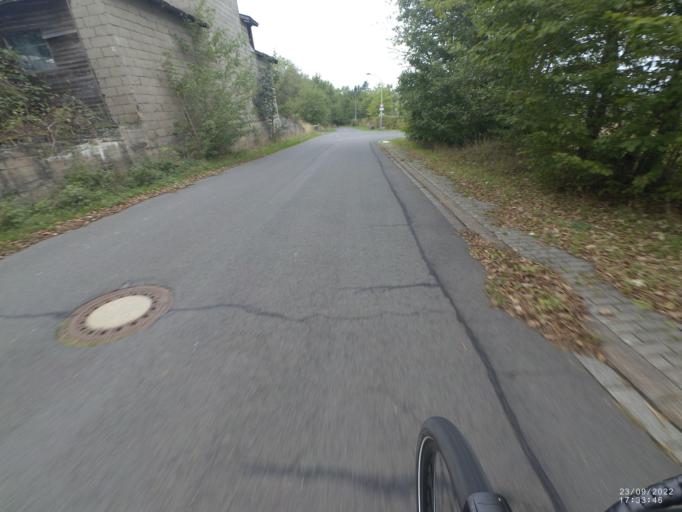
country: DE
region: Rheinland-Pfalz
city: Dockweiler
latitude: 50.2485
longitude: 6.7921
